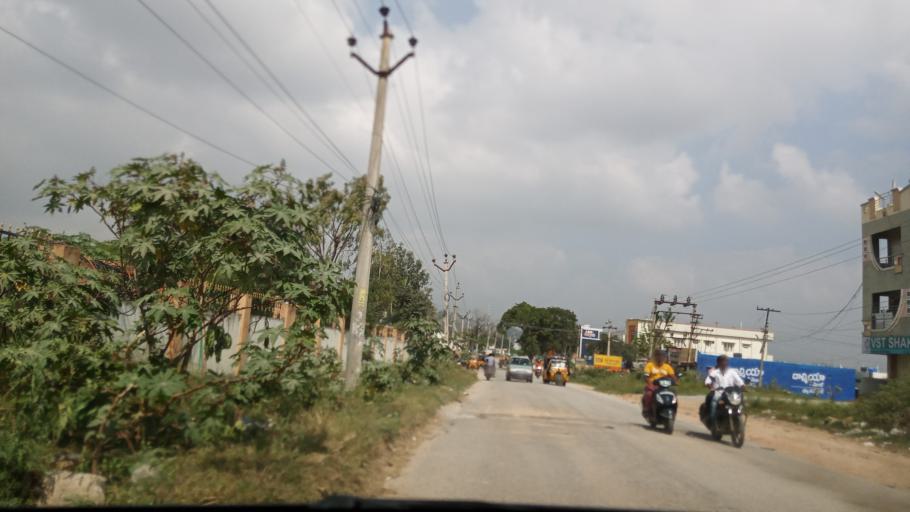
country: IN
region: Andhra Pradesh
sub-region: Chittoor
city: Madanapalle
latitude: 13.5680
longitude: 78.5144
